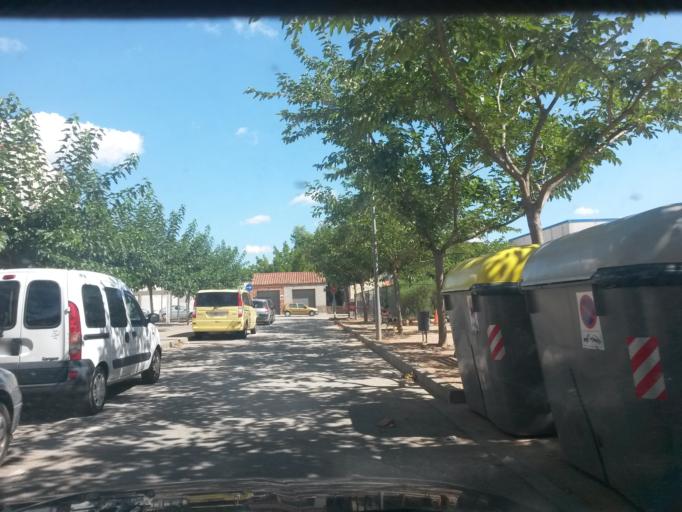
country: ES
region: Catalonia
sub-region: Provincia de Girona
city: Sarria de Ter
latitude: 42.0241
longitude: 2.8253
